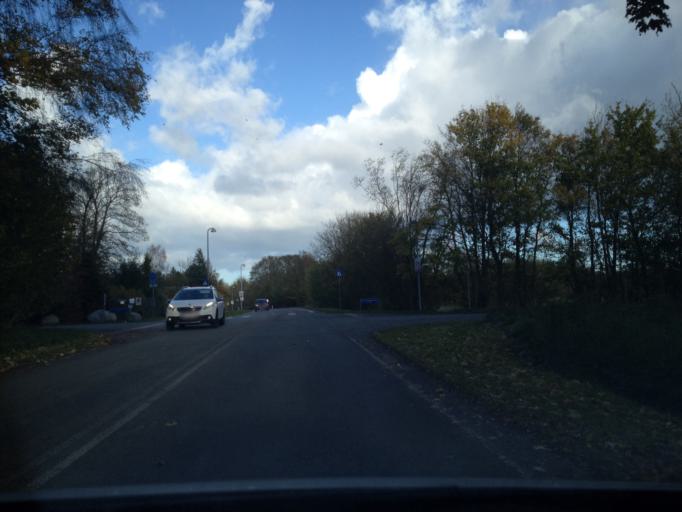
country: DK
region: Capital Region
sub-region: Fureso Kommune
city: Farum
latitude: 55.8268
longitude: 12.3703
